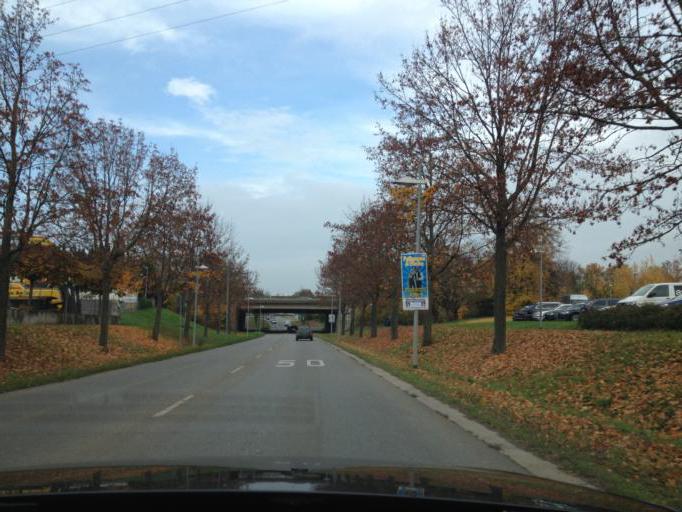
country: DE
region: Baden-Wuerttemberg
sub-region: Regierungsbezirk Stuttgart
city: Neckarsulm
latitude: 49.1808
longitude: 9.2240
